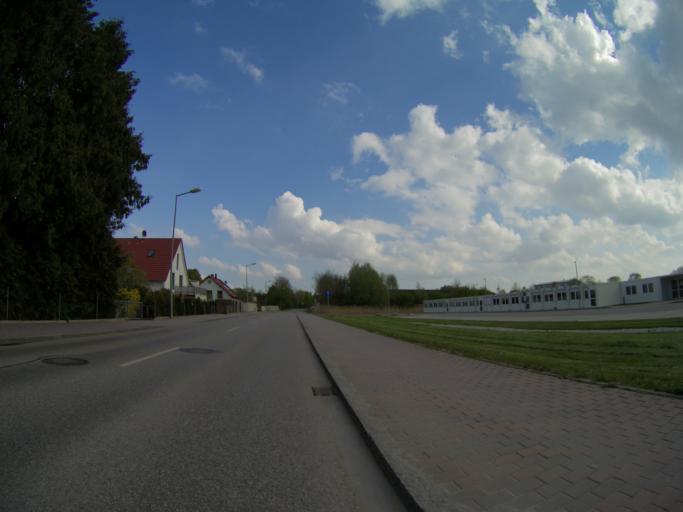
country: DE
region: Bavaria
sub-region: Upper Bavaria
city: Freising
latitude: 48.3871
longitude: 11.7662
